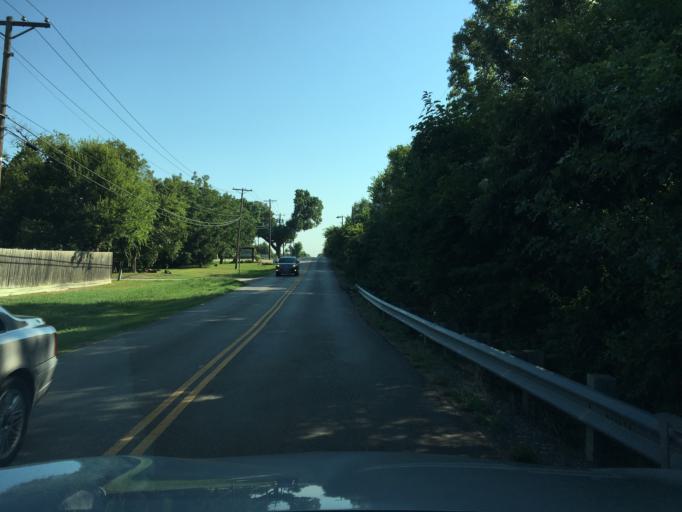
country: US
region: Texas
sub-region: Dallas County
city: Garland
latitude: 32.9612
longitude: -96.6597
